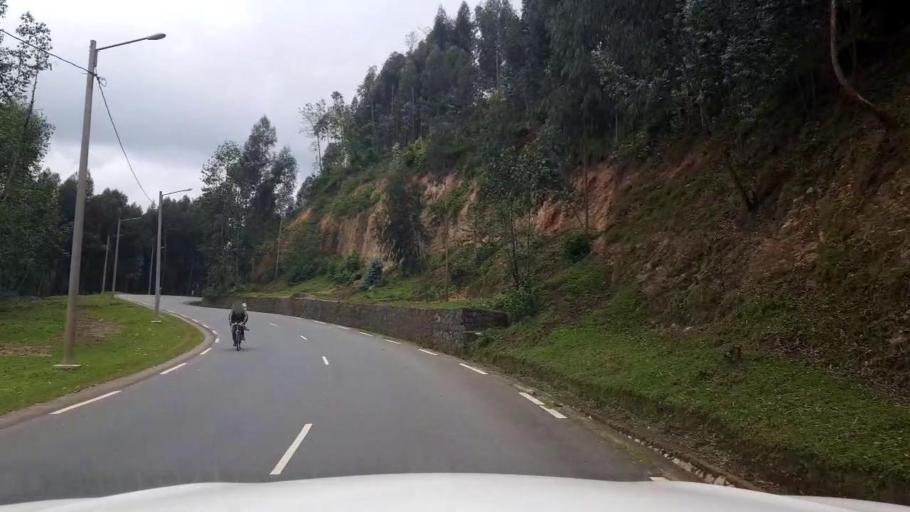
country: RW
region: Northern Province
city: Musanze
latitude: -1.6224
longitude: 29.5049
